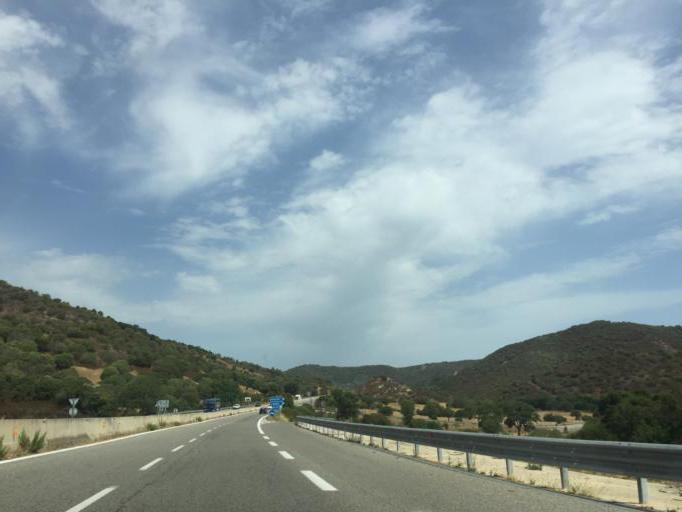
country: IT
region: Sardinia
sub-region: Provincia di Olbia-Tempio
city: Padru
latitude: 40.8158
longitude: 9.5840
